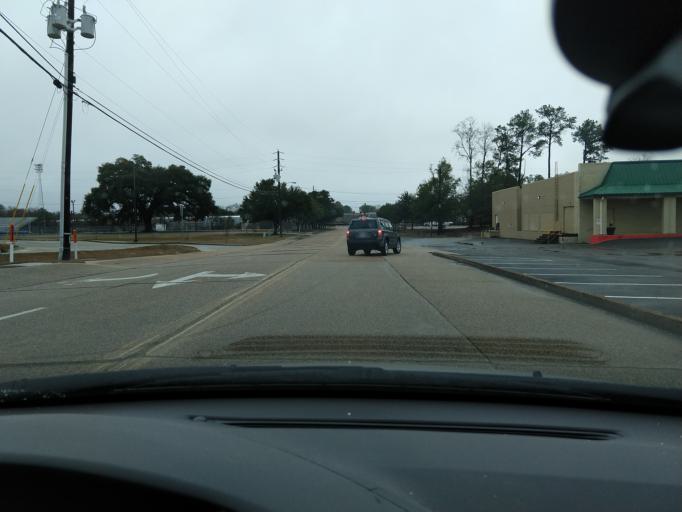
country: US
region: Mississippi
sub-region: Jackson County
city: Ocean Springs
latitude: 30.4143
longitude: -88.7955
